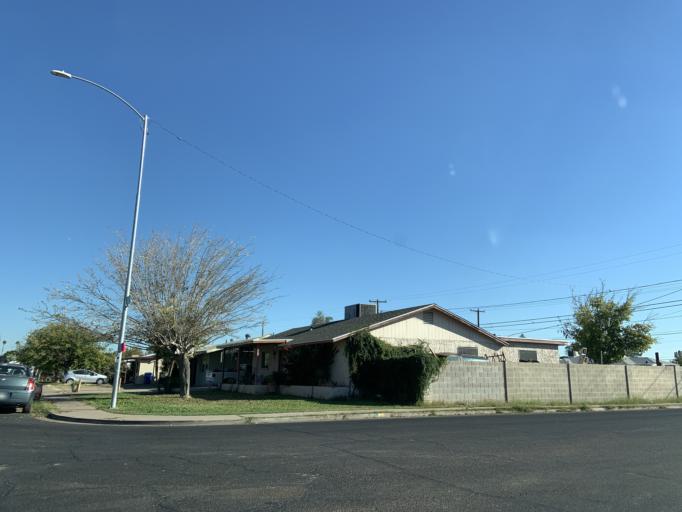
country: US
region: Arizona
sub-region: Maricopa County
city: Mesa
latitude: 33.4043
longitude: -111.8617
